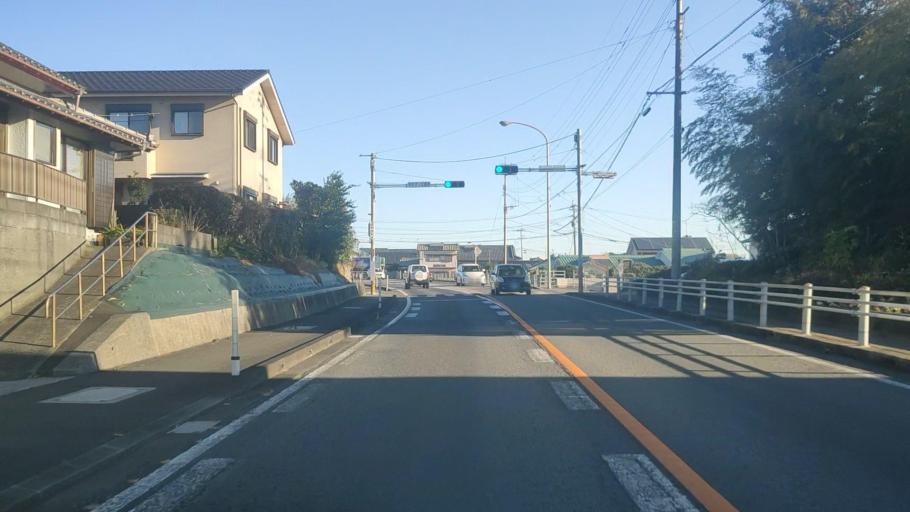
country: JP
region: Miyazaki
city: Nobeoka
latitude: 32.3714
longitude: 131.6302
